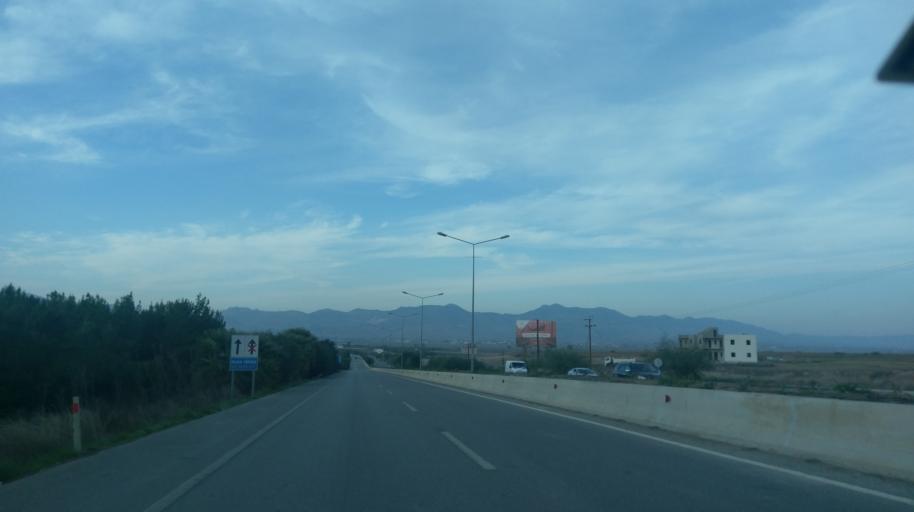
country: CY
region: Lefkosia
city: Geri
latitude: 35.1615
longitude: 33.5043
